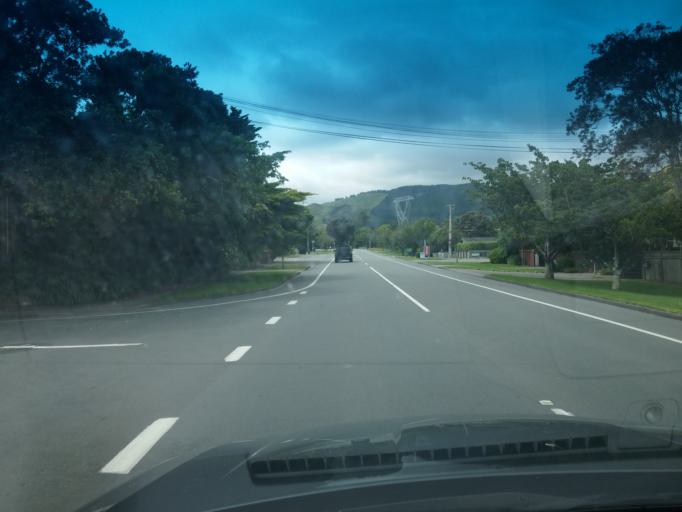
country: NZ
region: Wellington
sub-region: Kapiti Coast District
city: Paraparaumu
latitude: -40.8764
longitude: 175.0435
